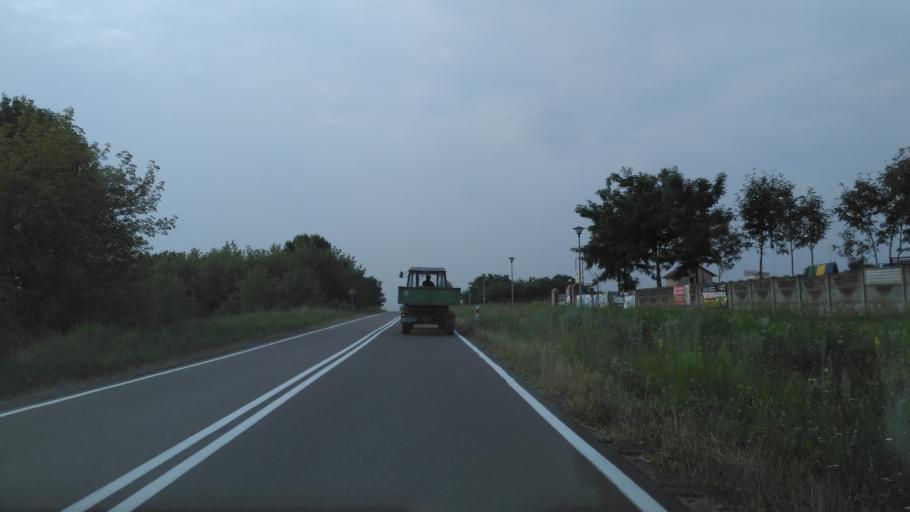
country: PL
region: Lublin Voivodeship
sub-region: Powiat chelmski
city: Rejowiec Fabryczny
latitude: 51.1819
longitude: 23.1747
